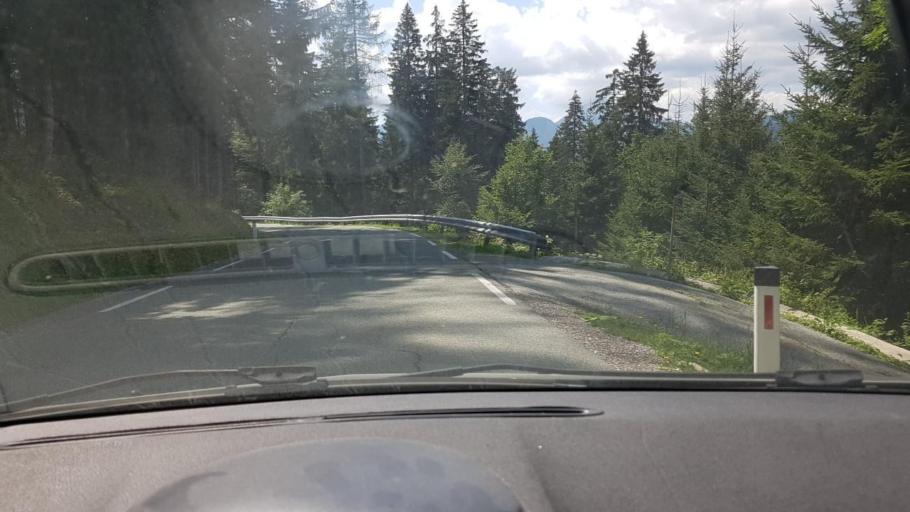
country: SI
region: Jezersko
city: Zgornje Jezersko
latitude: 46.4165
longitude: 14.5262
